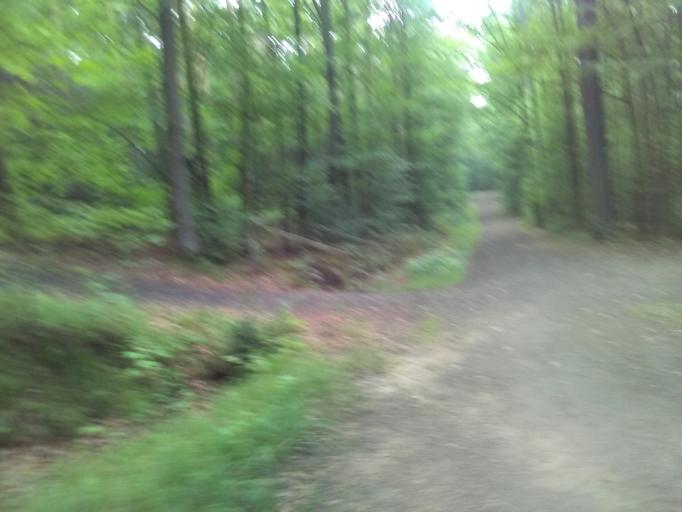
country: DE
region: Bavaria
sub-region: Upper Franconia
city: Bamberg
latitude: 49.8622
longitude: 10.9003
